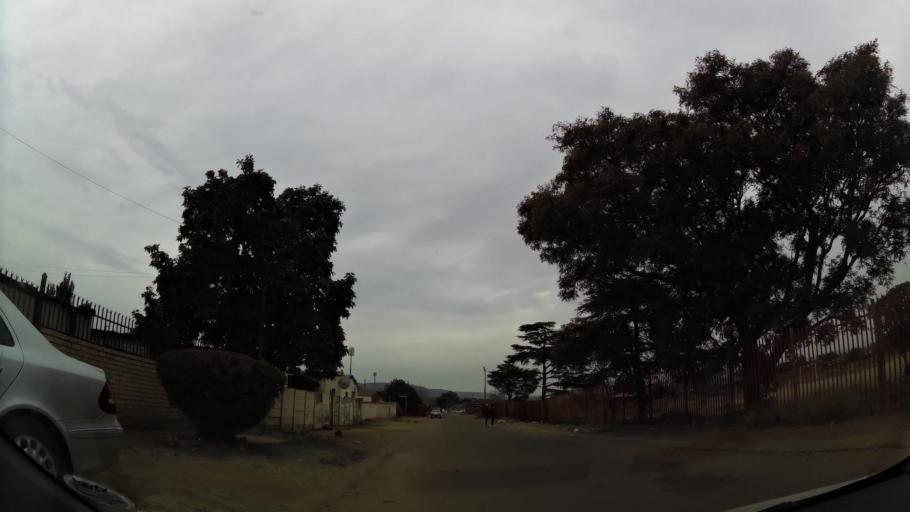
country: ZA
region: Gauteng
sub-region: City of Tshwane Metropolitan Municipality
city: Pretoria
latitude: -25.7099
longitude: 28.3350
